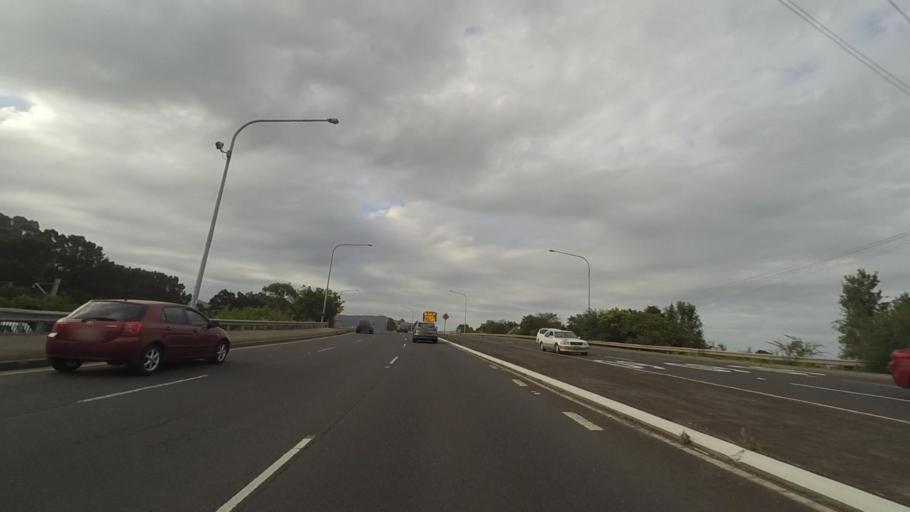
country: AU
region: New South Wales
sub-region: Wollongong
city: Gwynneville
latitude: -34.4104
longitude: 150.8923
